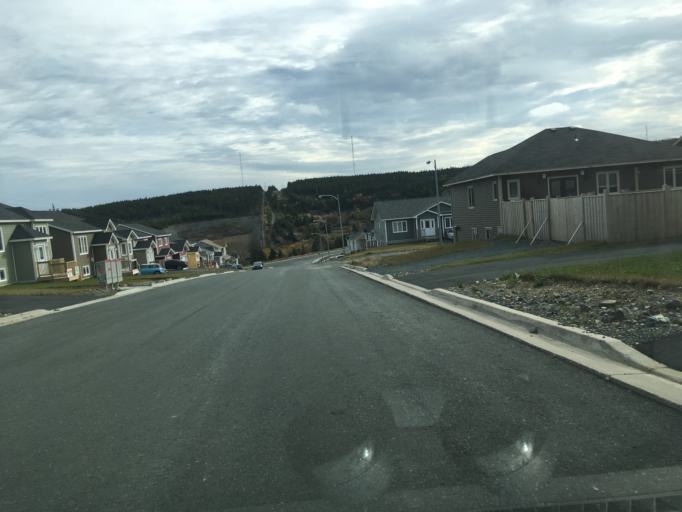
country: CA
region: Newfoundland and Labrador
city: Mount Pearl
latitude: 47.5517
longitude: -52.7844
